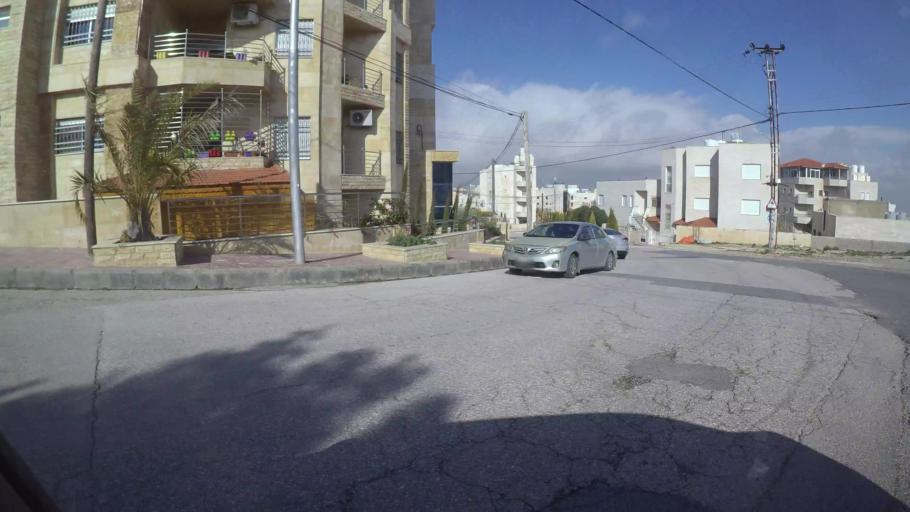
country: JO
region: Amman
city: Al Jubayhah
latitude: 32.0401
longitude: 35.8753
